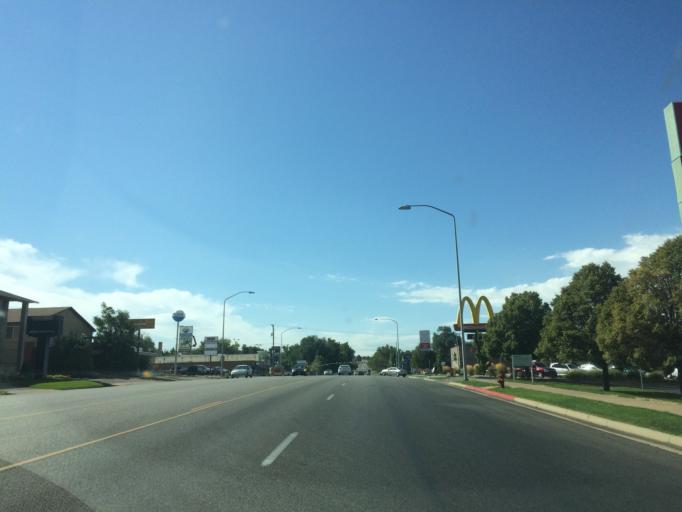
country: US
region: Utah
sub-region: Weber County
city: South Ogden
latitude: 41.1933
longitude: -111.9712
